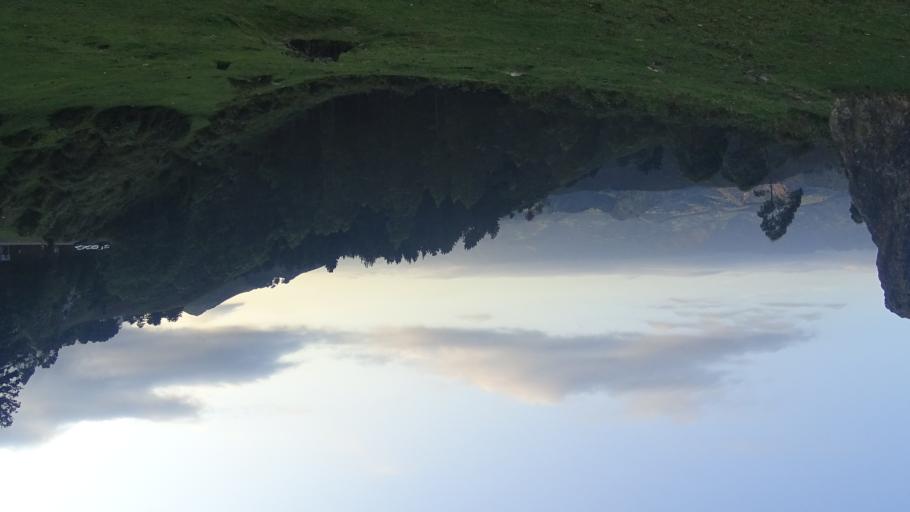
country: ES
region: Asturias
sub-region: Province of Asturias
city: Colunga
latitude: 43.4389
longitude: -5.1931
